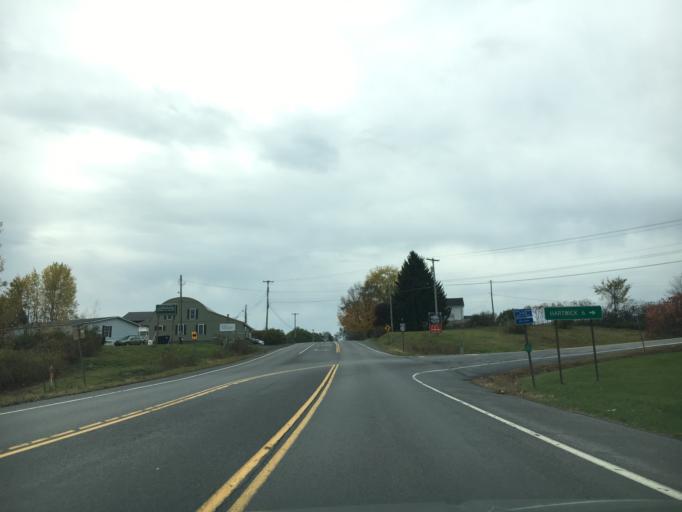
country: US
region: New York
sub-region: Otsego County
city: Cooperstown
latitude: 42.6647
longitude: -74.9590
